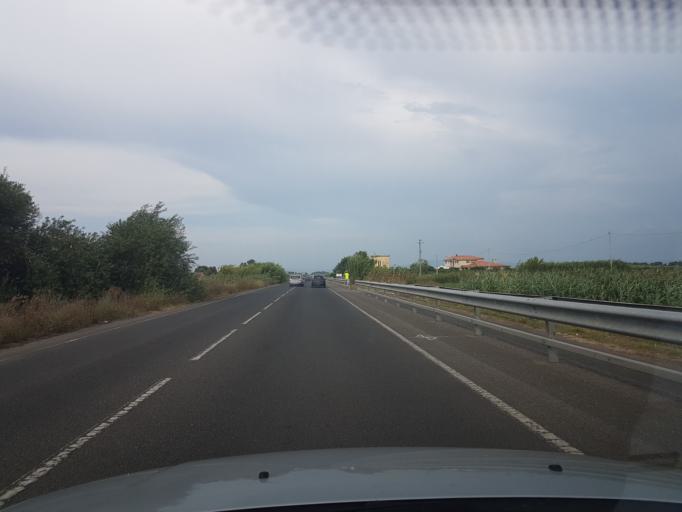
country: IT
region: Sardinia
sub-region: Provincia di Oristano
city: Cabras
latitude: 39.9107
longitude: 8.5299
